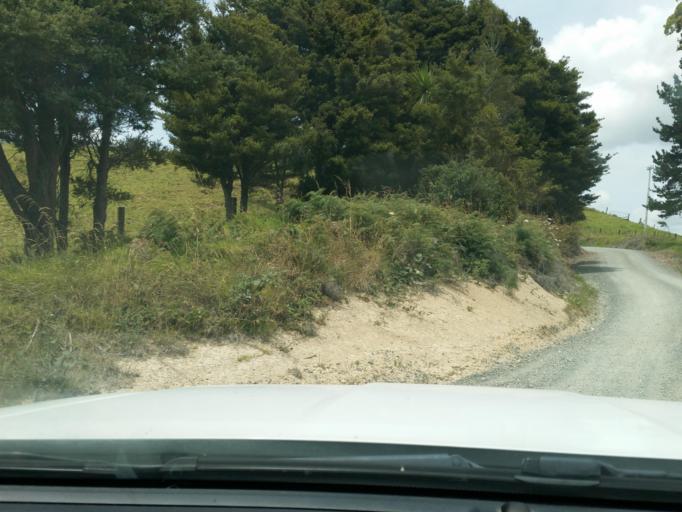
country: NZ
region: Northland
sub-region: Whangarei
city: Ruakaka
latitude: -35.9734
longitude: 174.2394
